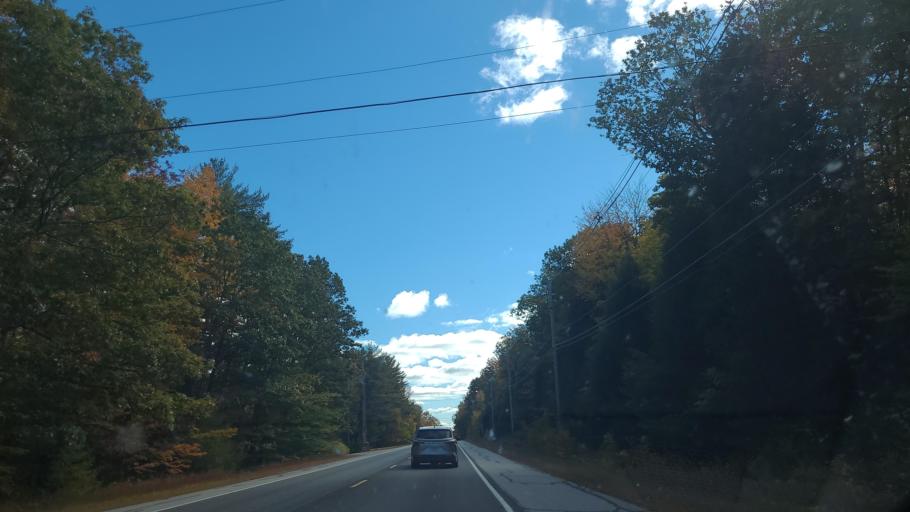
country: US
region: Maine
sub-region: Cumberland County
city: Bridgton
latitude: 43.9815
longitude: -70.6300
